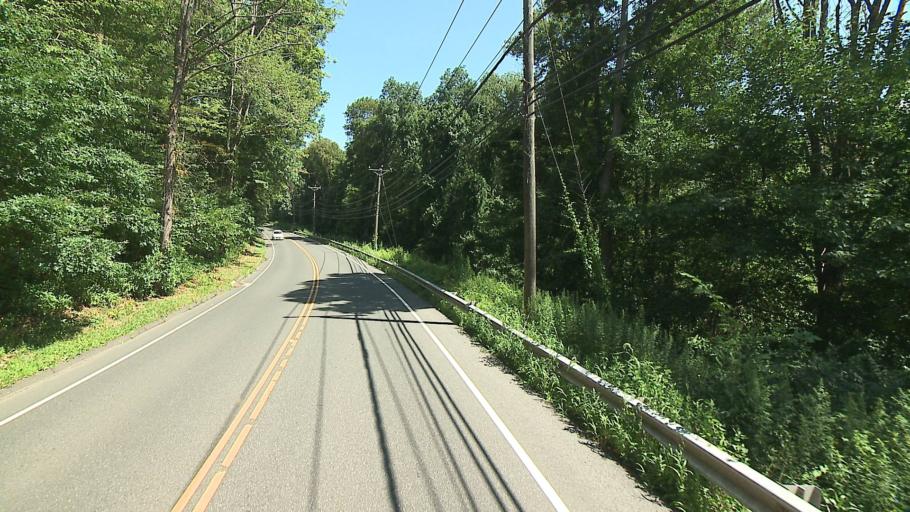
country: US
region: Connecticut
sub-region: New Haven County
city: Oxford
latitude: 41.3590
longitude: -73.1931
